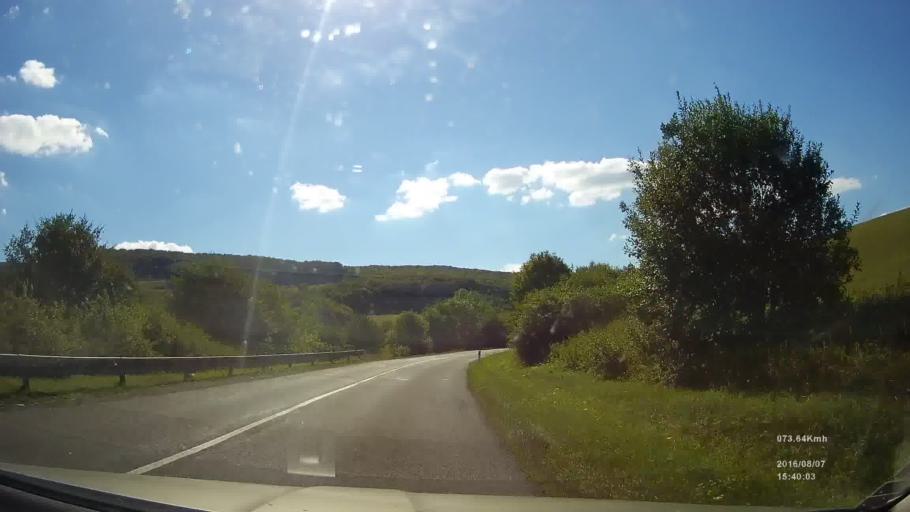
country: SK
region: Presovsky
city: Giraltovce
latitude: 49.1172
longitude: 21.5967
